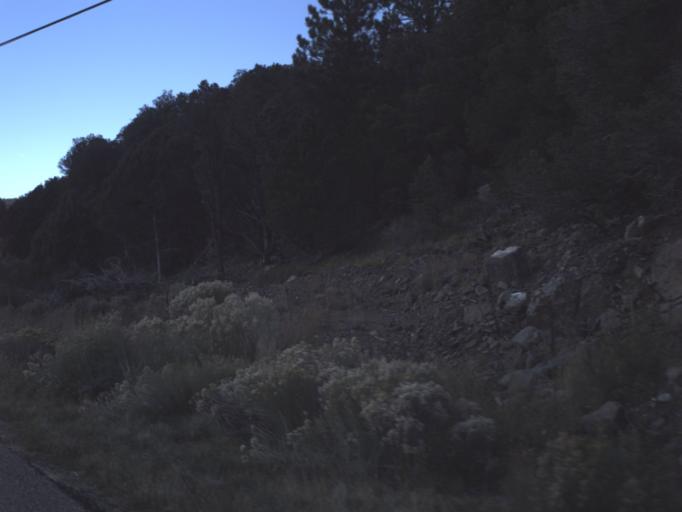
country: US
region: Utah
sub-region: Garfield County
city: Panguitch
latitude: 37.7674
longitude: -112.4662
